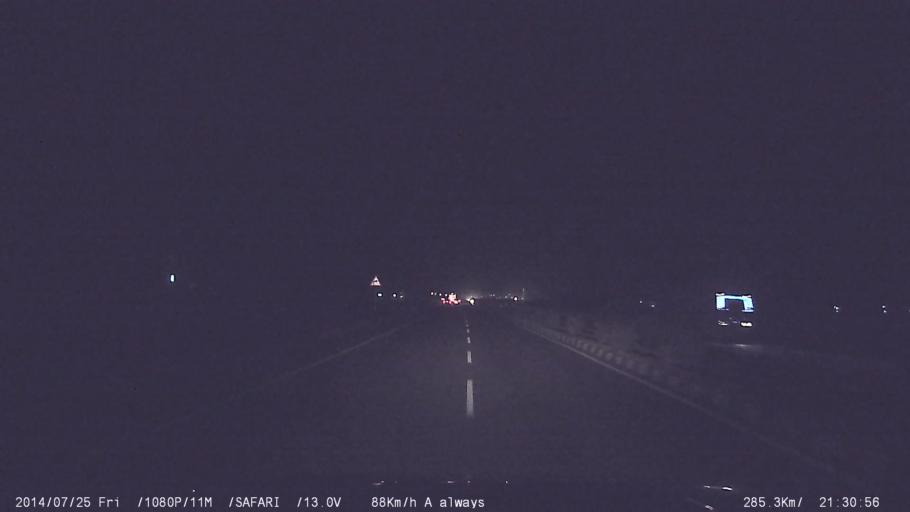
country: IN
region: Tamil Nadu
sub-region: Erode
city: Vijayapuri
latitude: 11.2407
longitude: 77.5114
